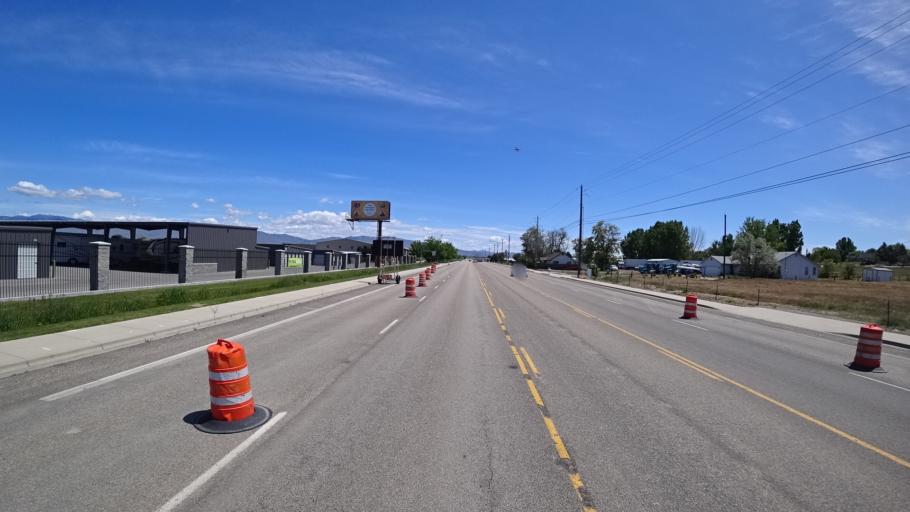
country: US
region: Idaho
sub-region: Ada County
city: Garden City
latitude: 43.5756
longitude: -116.2683
